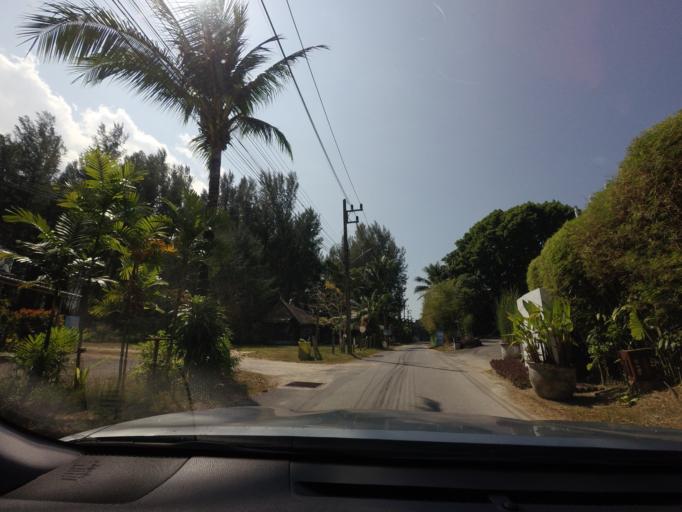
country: TH
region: Phangnga
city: Ban Khao Lak
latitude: 8.6633
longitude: 98.2471
